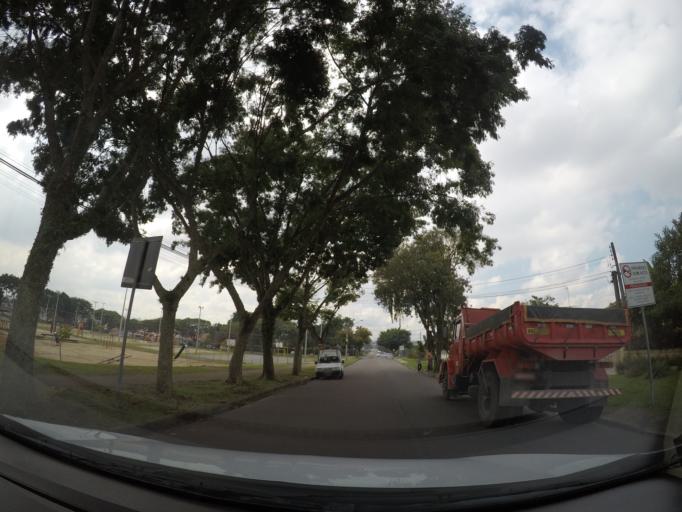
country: BR
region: Parana
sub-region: Curitiba
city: Curitiba
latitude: -25.4831
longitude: -49.2560
